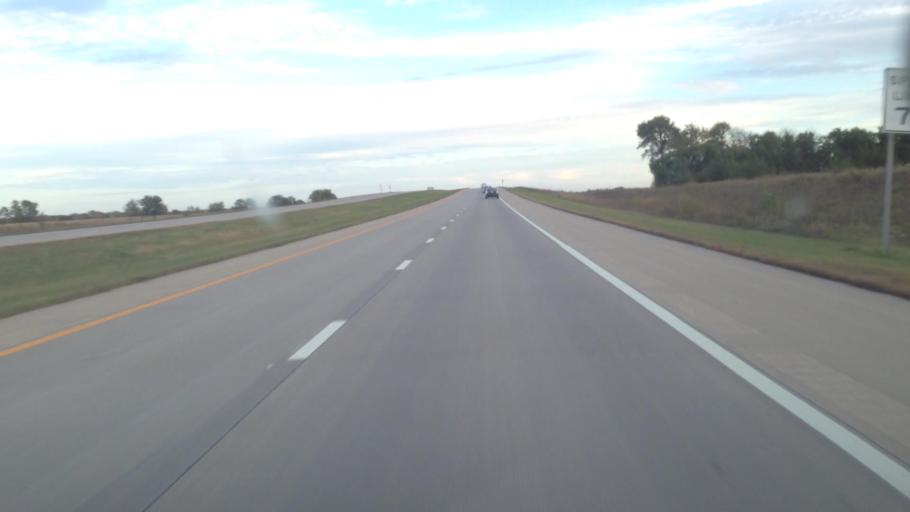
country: US
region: Kansas
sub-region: Franklin County
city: Ottawa
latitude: 38.6575
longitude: -95.2408
